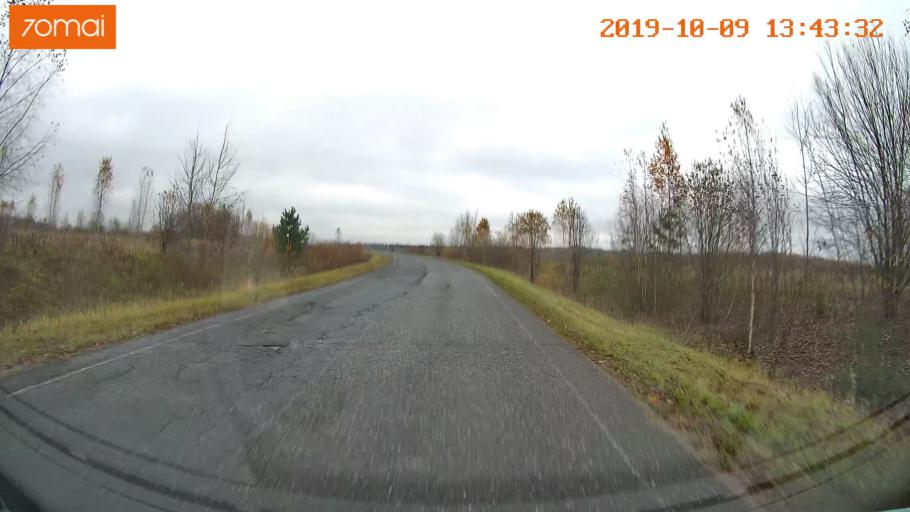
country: RU
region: Kostroma
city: Buy
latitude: 58.3578
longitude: 41.2011
